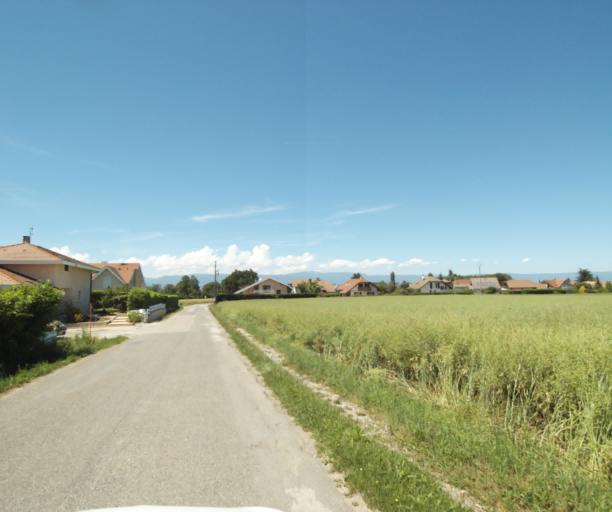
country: FR
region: Rhone-Alpes
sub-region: Departement de la Haute-Savoie
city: Veigy-Foncenex
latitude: 46.2617
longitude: 6.2583
